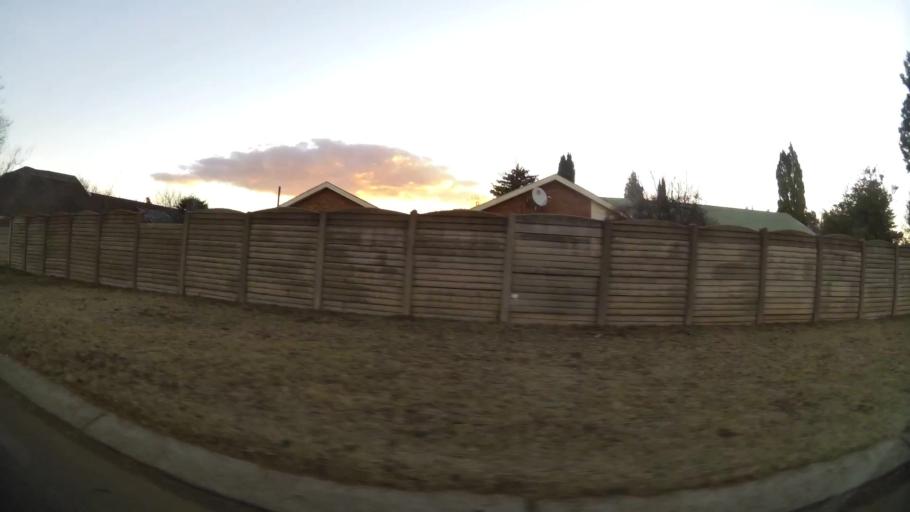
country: ZA
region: North-West
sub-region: Dr Kenneth Kaunda District Municipality
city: Potchefstroom
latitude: -26.7149
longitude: 27.1235
